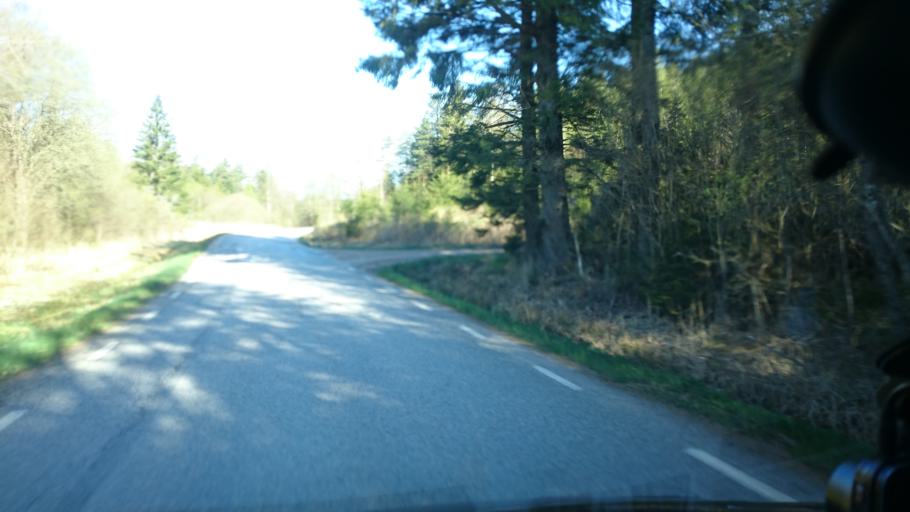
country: SE
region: Vaestra Goetaland
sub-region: Munkedals Kommun
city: Munkedal
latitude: 58.3690
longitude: 11.6931
